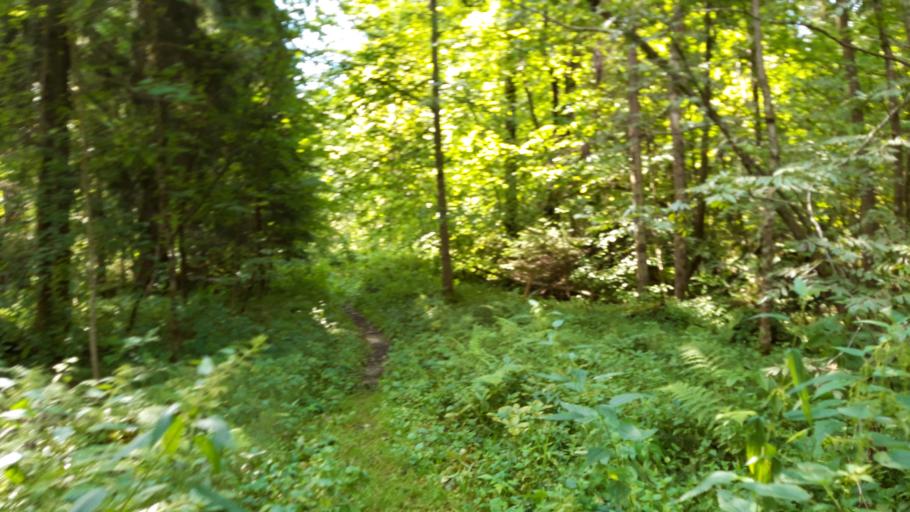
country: RU
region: Tverskaya
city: Konakovo
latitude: 56.6894
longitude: 36.7067
